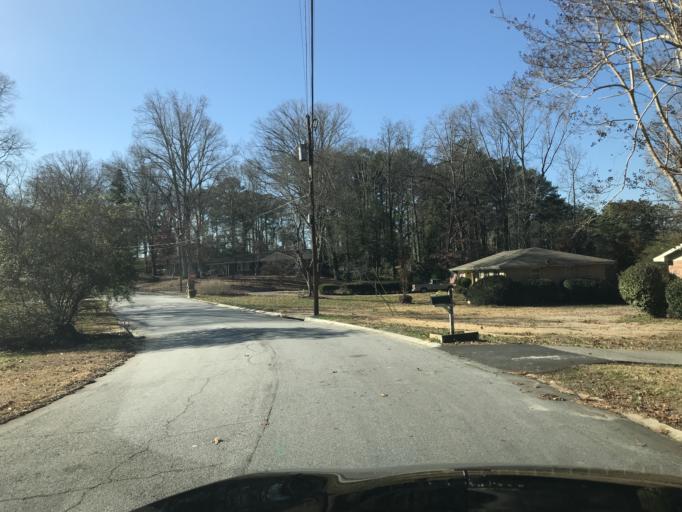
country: US
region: Georgia
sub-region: Clayton County
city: Riverdale
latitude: 33.5736
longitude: -84.3763
